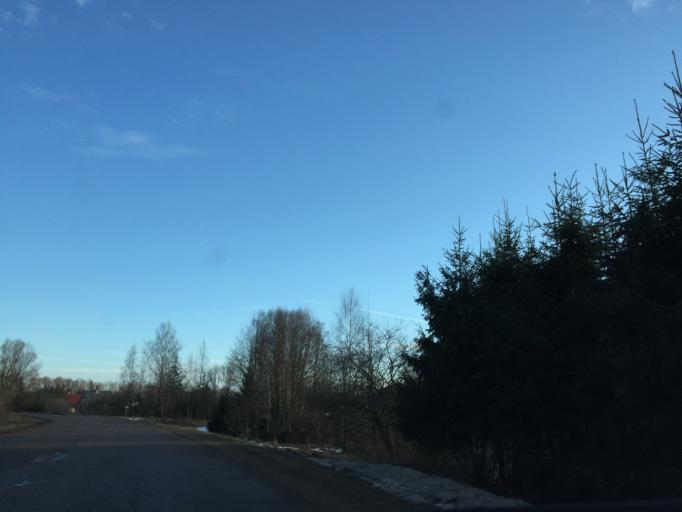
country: LV
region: Lecava
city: Iecava
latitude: 56.6922
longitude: 24.0892
